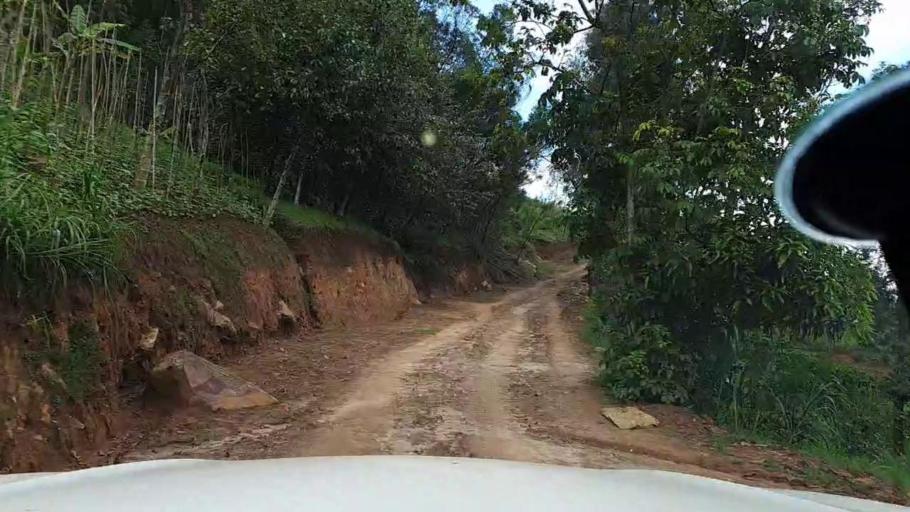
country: RW
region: Southern Province
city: Gitarama
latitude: -1.8073
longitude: 29.8006
